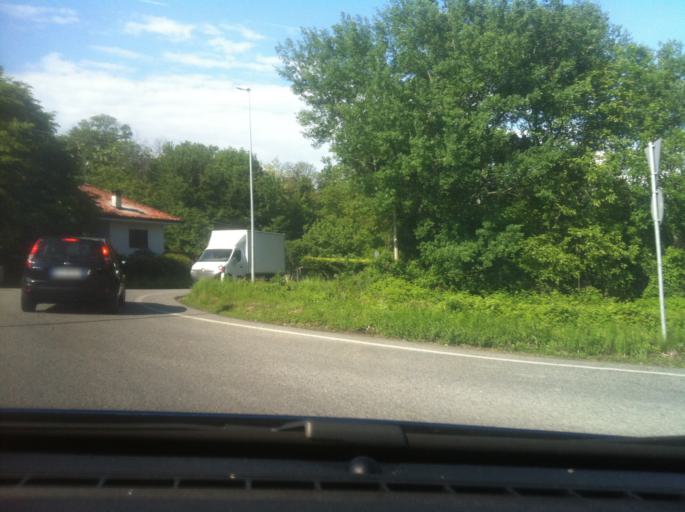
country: IT
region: Piedmont
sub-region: Provincia di Torino
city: Torre Canavese
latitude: 45.3938
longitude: 7.7553
